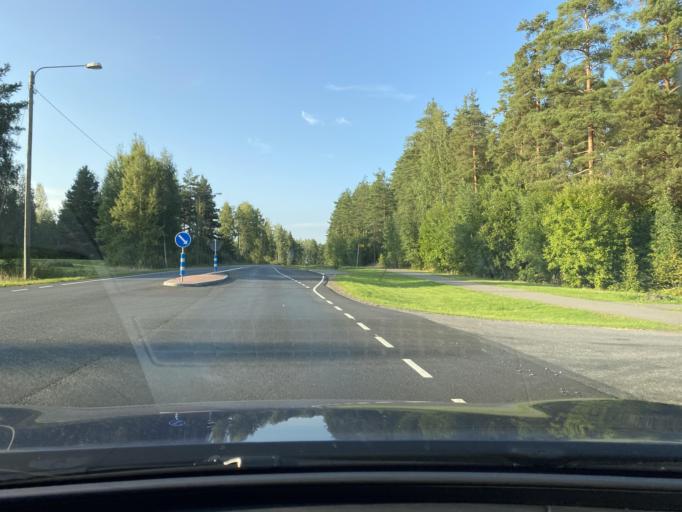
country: FI
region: Kymenlaakso
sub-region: Kouvola
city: Kouvola
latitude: 60.8939
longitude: 26.6043
